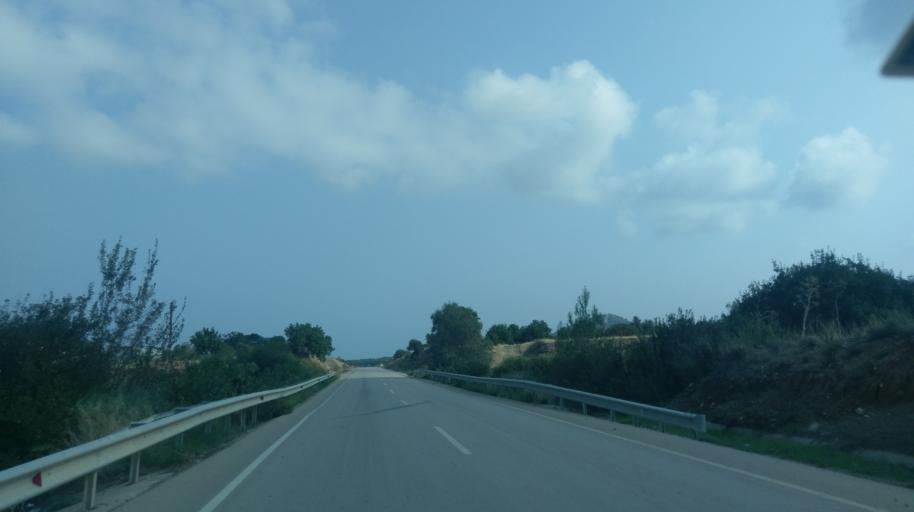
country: CY
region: Ammochostos
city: Lefkonoiko
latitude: 35.3940
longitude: 33.7509
